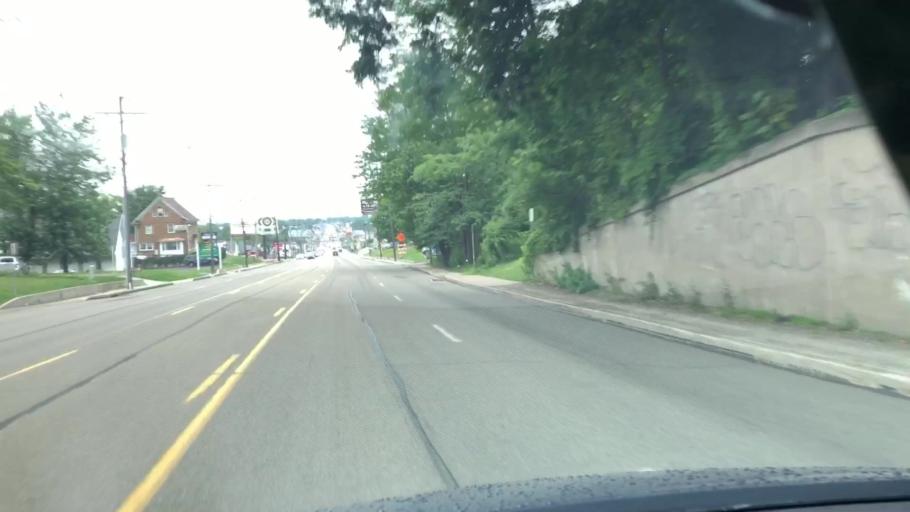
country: US
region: Pennsylvania
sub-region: Erie County
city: Erie
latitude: 42.0847
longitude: -80.0882
